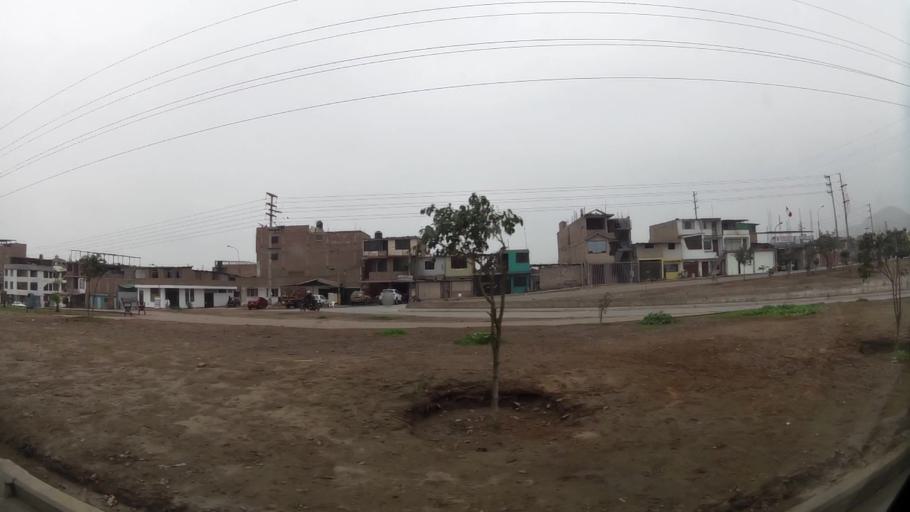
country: PE
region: Lima
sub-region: Lima
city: Surco
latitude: -12.1983
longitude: -76.9399
